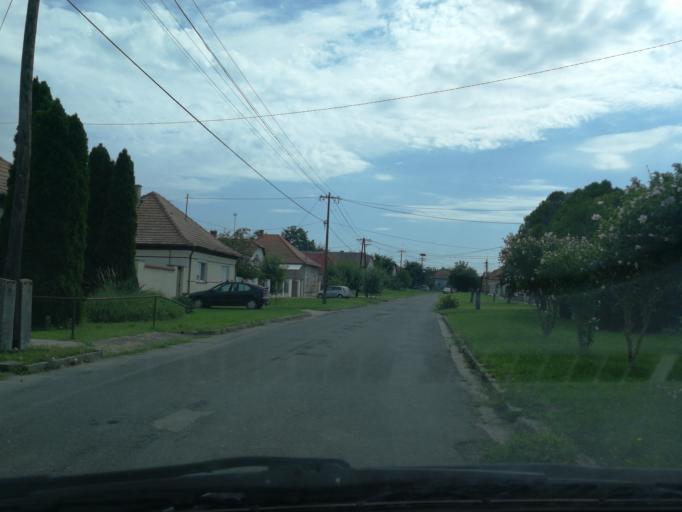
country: HU
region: Bacs-Kiskun
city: Hercegszanto
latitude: 45.9520
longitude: 18.9303
